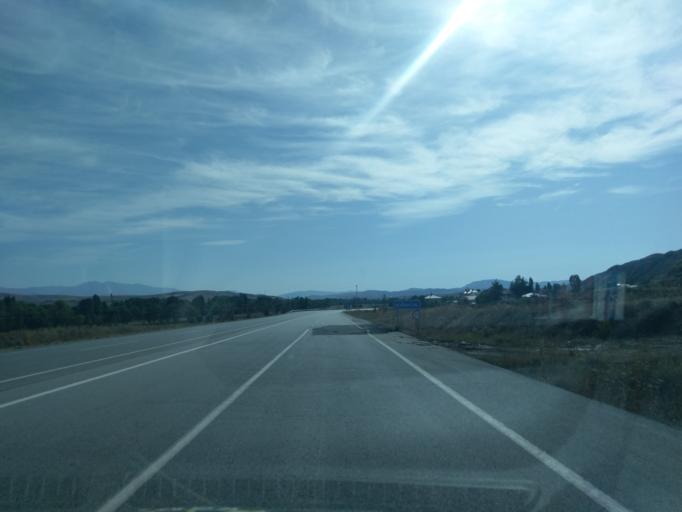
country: TR
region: Sivas
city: Imranli
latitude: 39.8829
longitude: 38.0626
